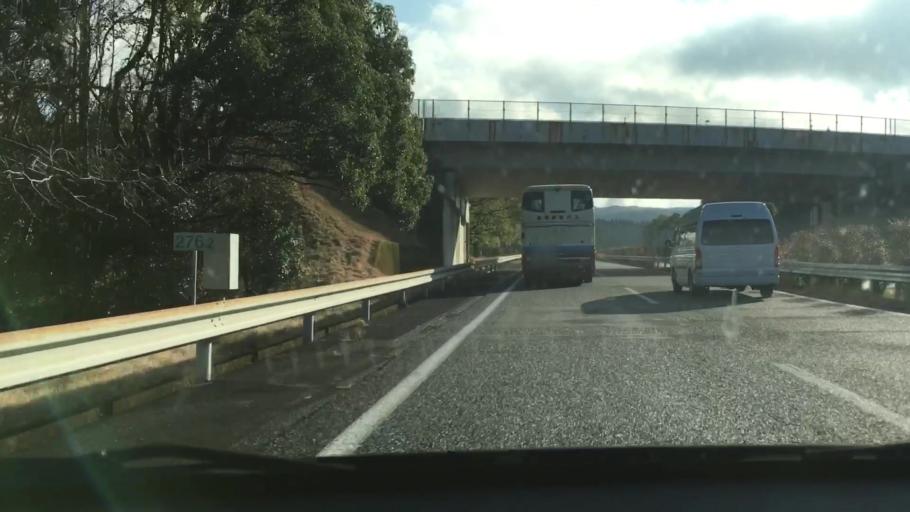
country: JP
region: Kagoshima
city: Okuchi-shinohara
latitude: 32.0335
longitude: 130.7984
